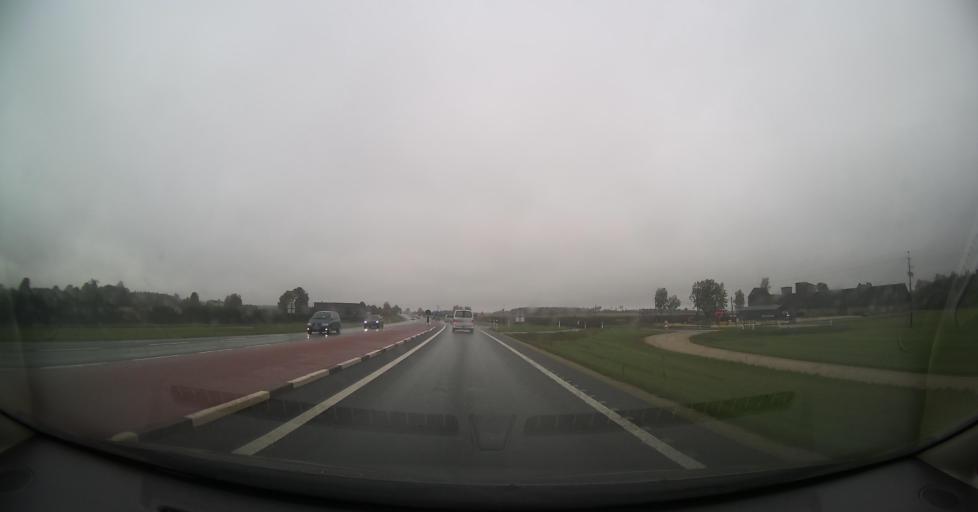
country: EE
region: Jogevamaa
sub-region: Poltsamaa linn
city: Poltsamaa
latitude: 58.6394
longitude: 26.0921
